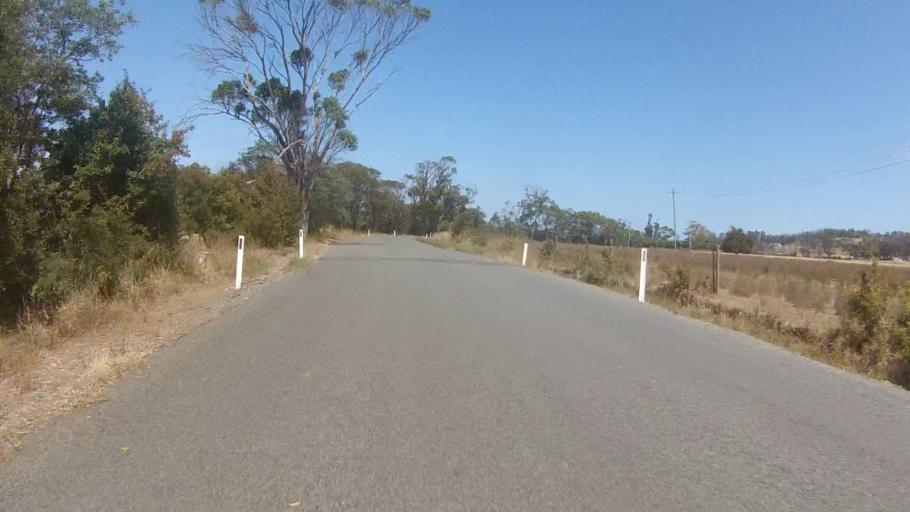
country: AU
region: Tasmania
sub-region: Sorell
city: Sorell
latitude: -42.8625
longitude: 147.8338
